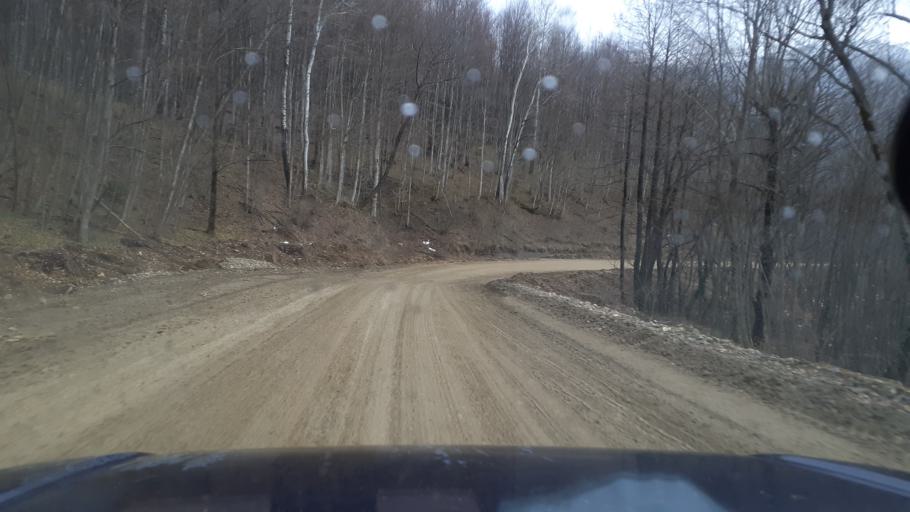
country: RU
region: Krasnodarskiy
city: Neftegorsk
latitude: 44.1653
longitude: 39.8097
